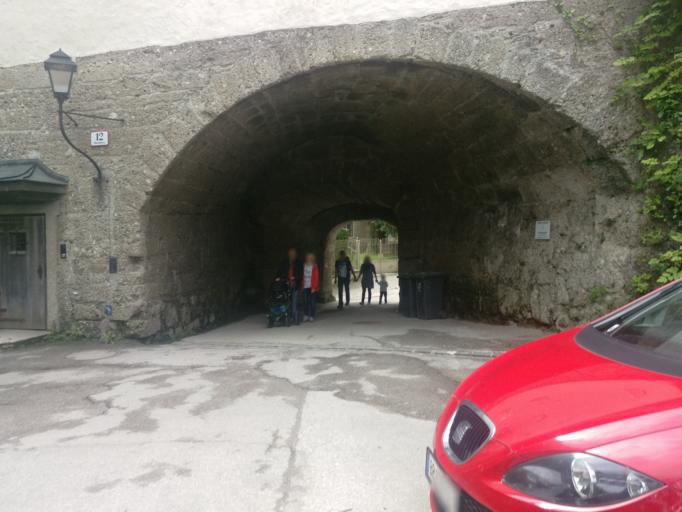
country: AT
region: Salzburg
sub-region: Salzburg Stadt
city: Salzburg
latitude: 47.7954
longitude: 13.0461
